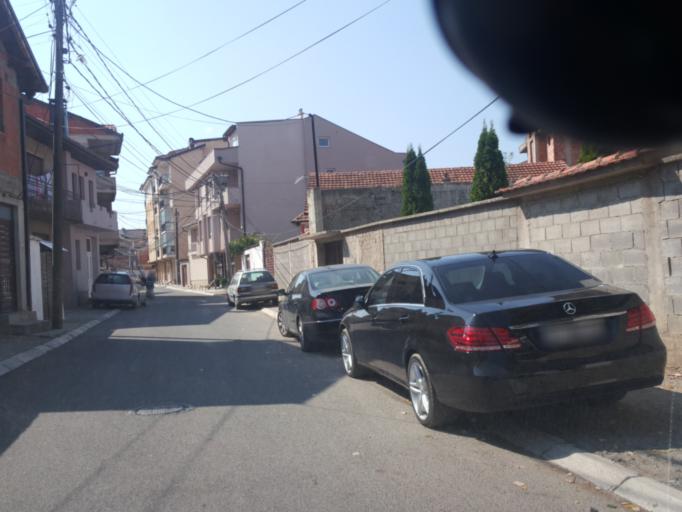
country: XK
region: Gjakova
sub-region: Komuna e Gjakoves
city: Gjakove
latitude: 42.3794
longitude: 20.4332
